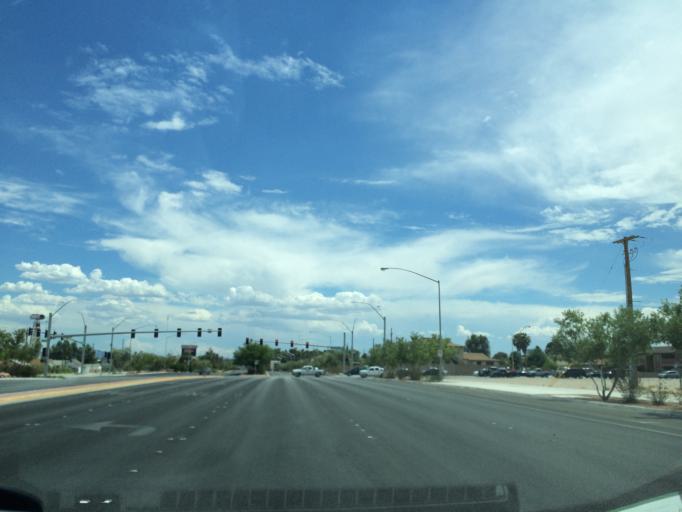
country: US
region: Nevada
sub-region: Clark County
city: North Las Vegas
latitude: 36.1969
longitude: -115.1341
